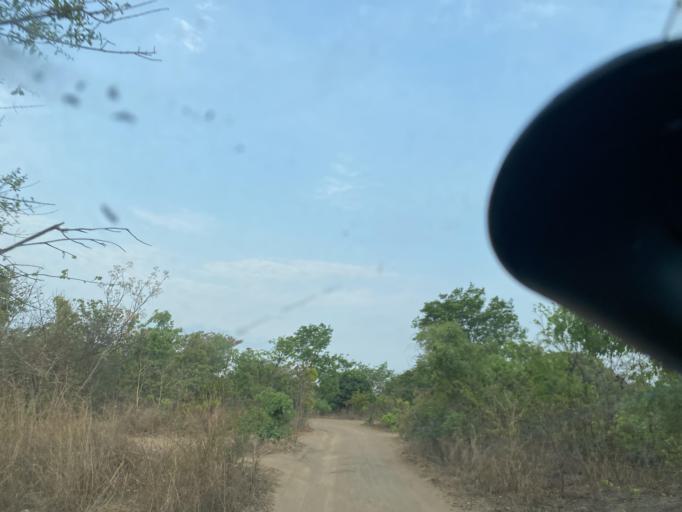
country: ZM
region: Lusaka
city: Chongwe
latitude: -15.2080
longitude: 28.5099
